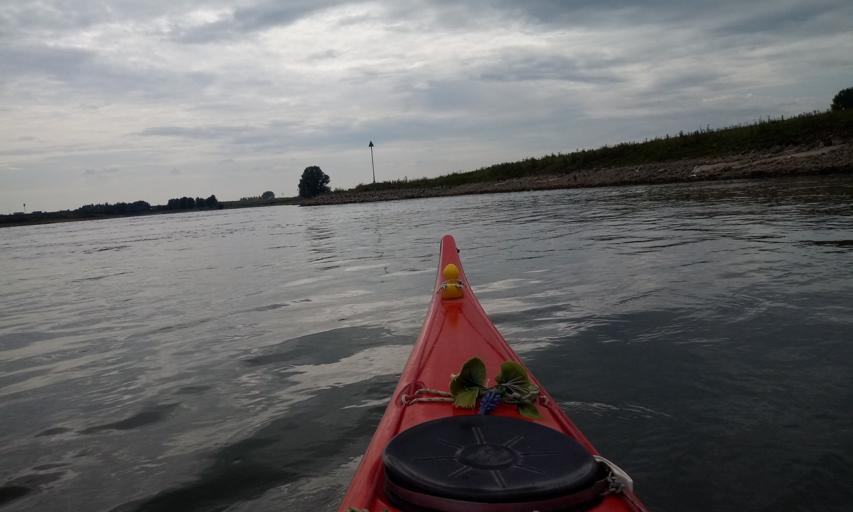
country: NL
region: Overijssel
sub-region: Gemeente Deventer
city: Deventer
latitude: 52.2422
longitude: 6.1629
